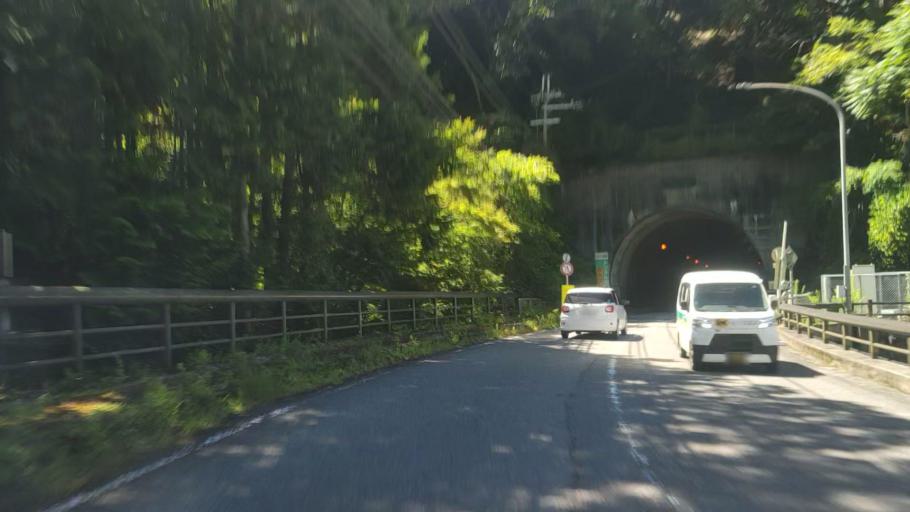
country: JP
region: Nara
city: Yoshino-cho
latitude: 34.3478
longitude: 135.9371
